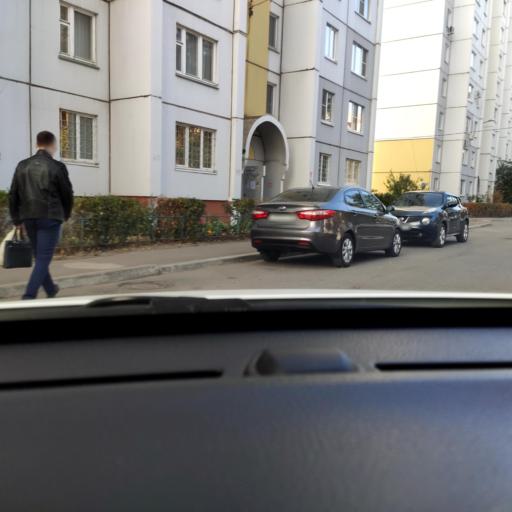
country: RU
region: Voronezj
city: Voronezh
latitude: 51.6873
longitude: 39.2820
